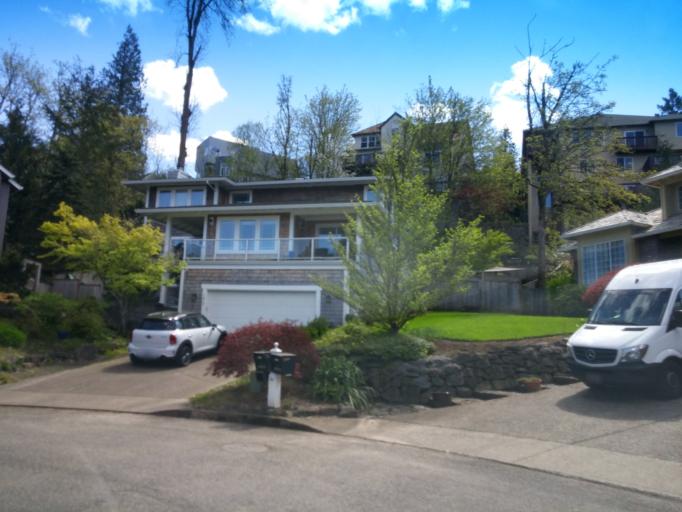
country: US
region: Oregon
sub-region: Washington County
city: West Haven
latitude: 45.5350
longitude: -122.7798
